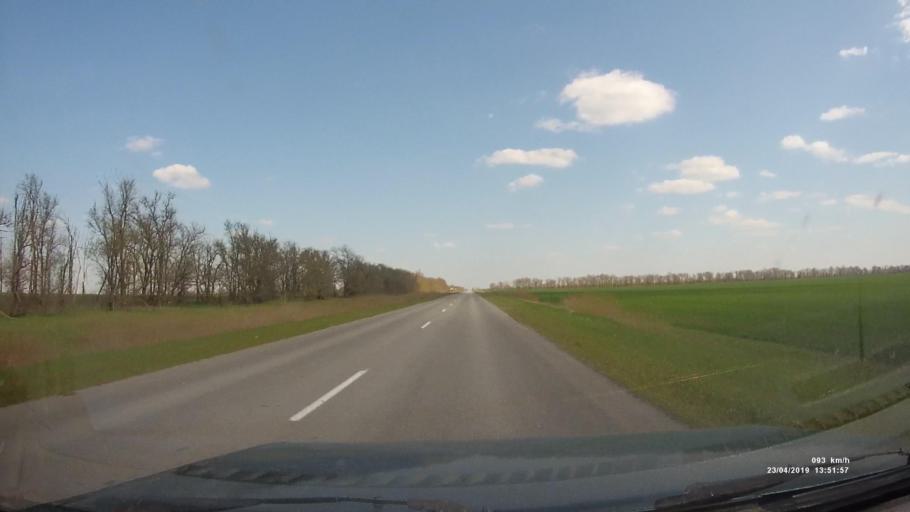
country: RU
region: Rostov
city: Remontnoye
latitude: 46.6005
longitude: 42.9441
